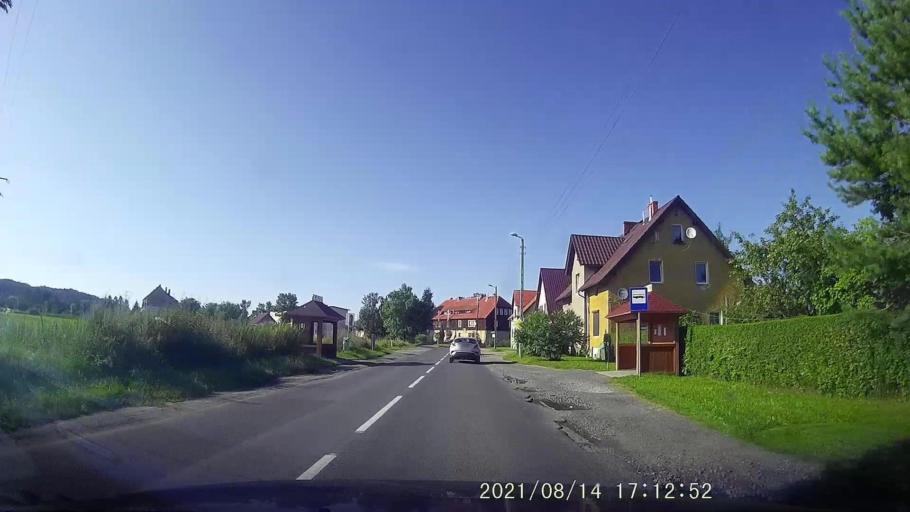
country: PL
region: Lower Silesian Voivodeship
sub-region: Powiat jeleniogorski
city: Myslakowice
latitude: 50.8459
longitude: 15.7861
